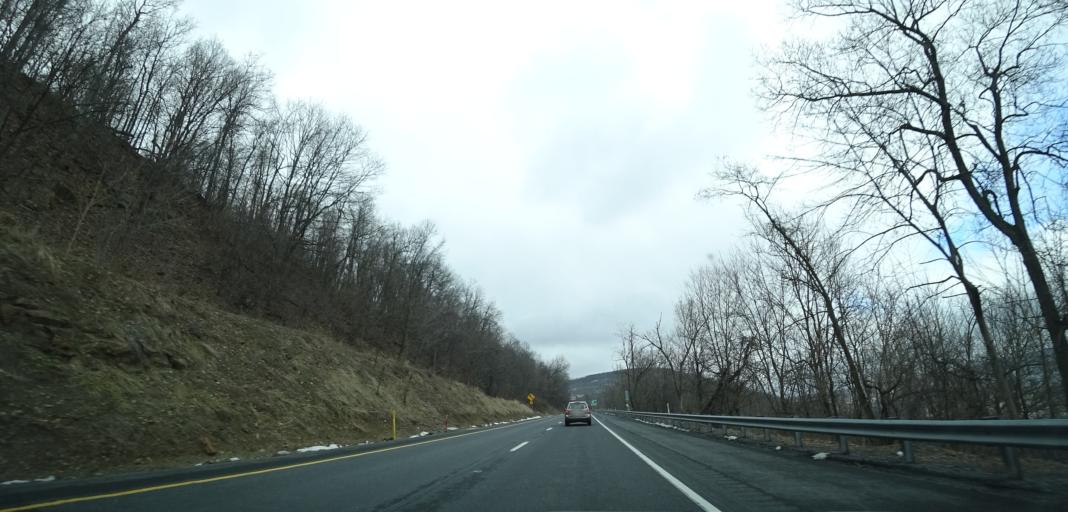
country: US
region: Pennsylvania
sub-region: Bedford County
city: Earlston
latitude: 39.8784
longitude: -78.2468
